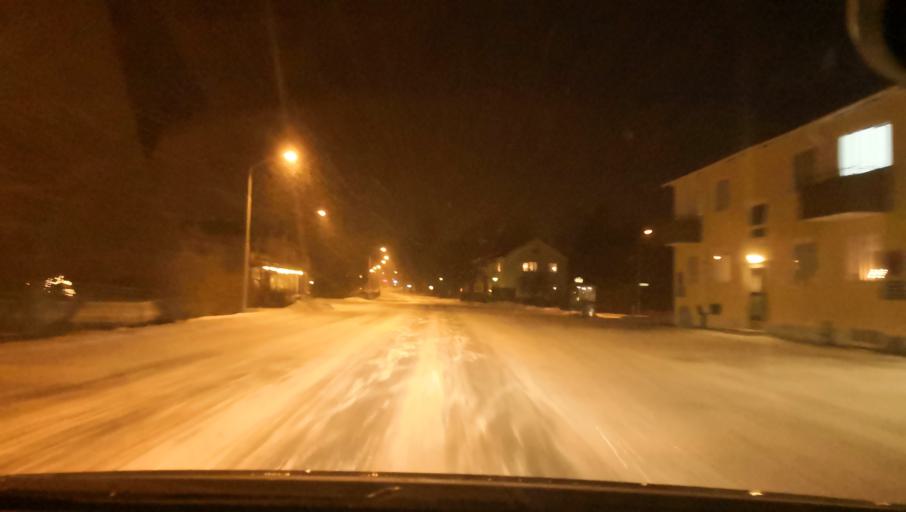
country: SE
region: Uppsala
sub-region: Heby Kommun
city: Tarnsjo
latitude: 60.1575
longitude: 16.9336
